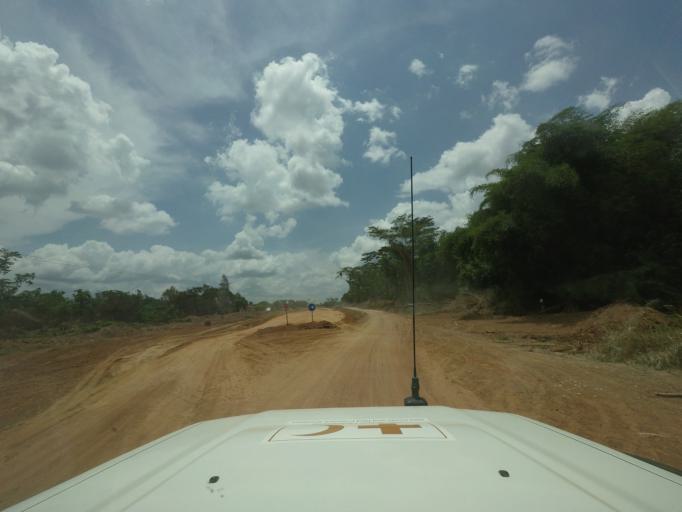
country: LR
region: Nimba
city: Sanniquellie
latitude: 7.2410
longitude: -8.8760
